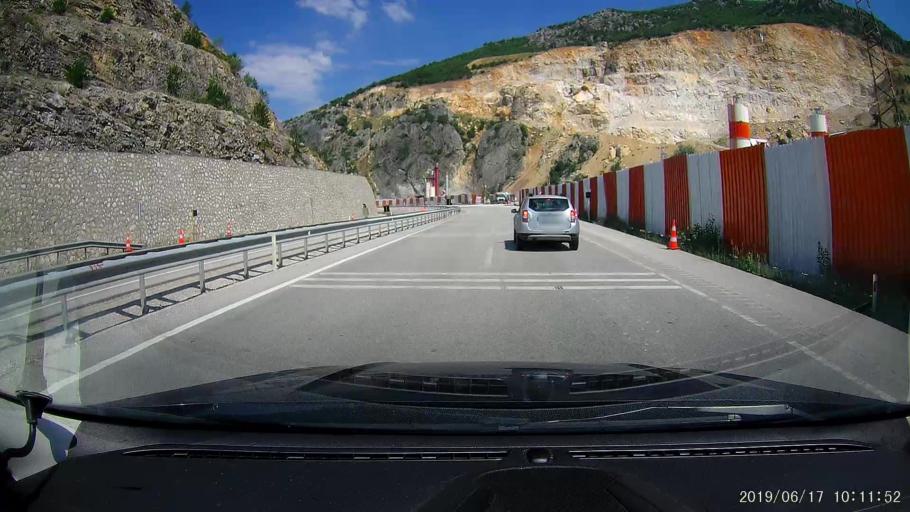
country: TR
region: Amasya
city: Saraycik
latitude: 40.9752
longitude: 35.0808
